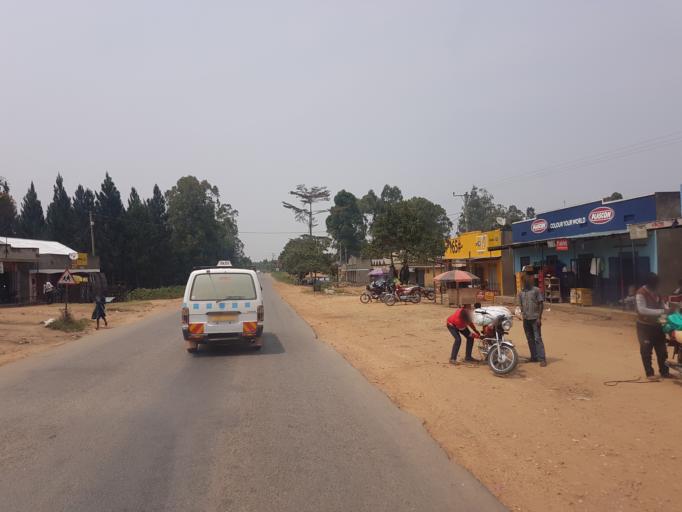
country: UG
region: Western Region
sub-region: Bushenyi District
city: Bushenyi
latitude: -0.5406
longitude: 30.1671
